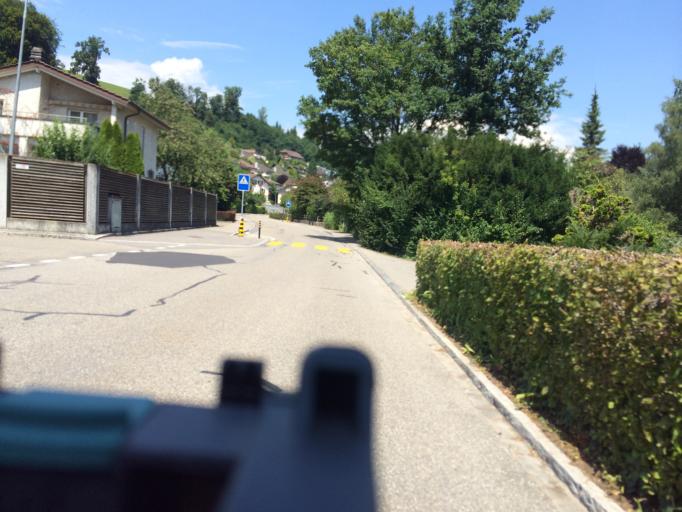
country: CH
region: Bern
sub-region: Bern-Mittelland District
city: Zollikofen
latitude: 46.9802
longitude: 7.4403
